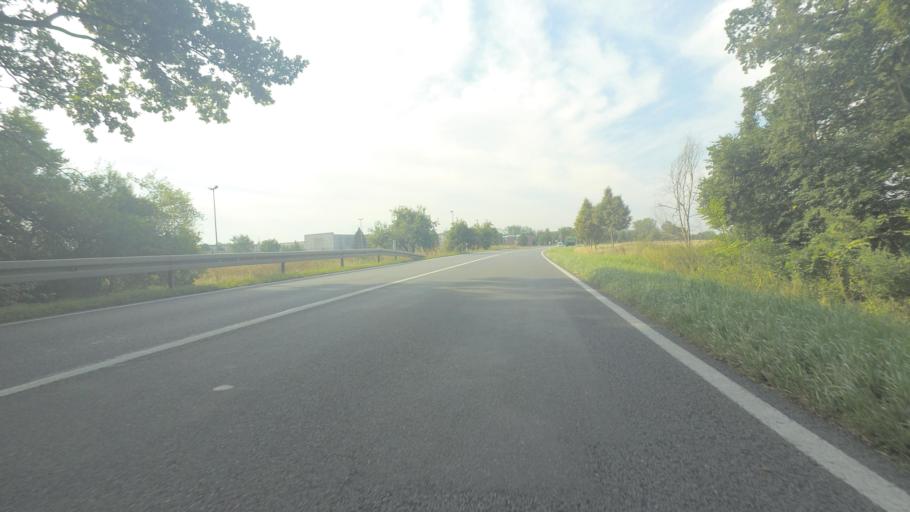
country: DE
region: Mecklenburg-Vorpommern
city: Borrentin
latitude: 53.7400
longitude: 12.9281
